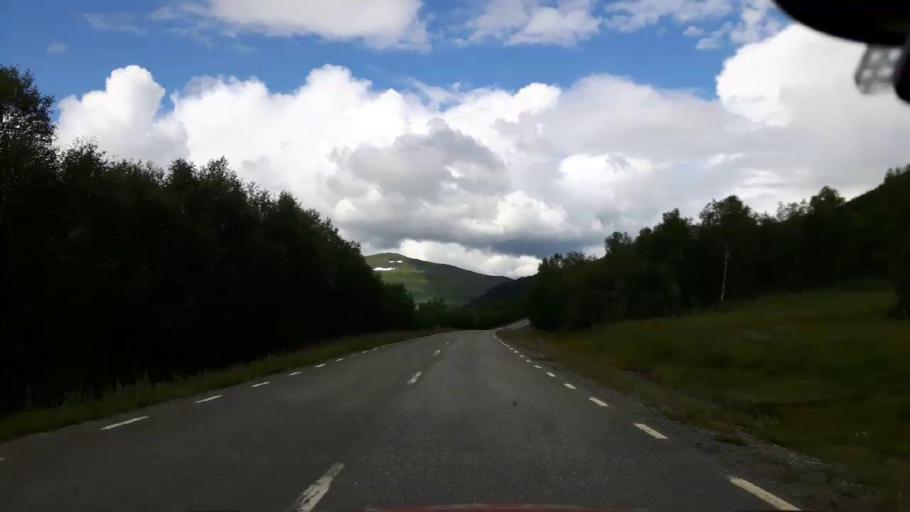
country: NO
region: Nordland
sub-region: Hattfjelldal
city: Hattfjelldal
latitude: 65.0625
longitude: 14.7009
